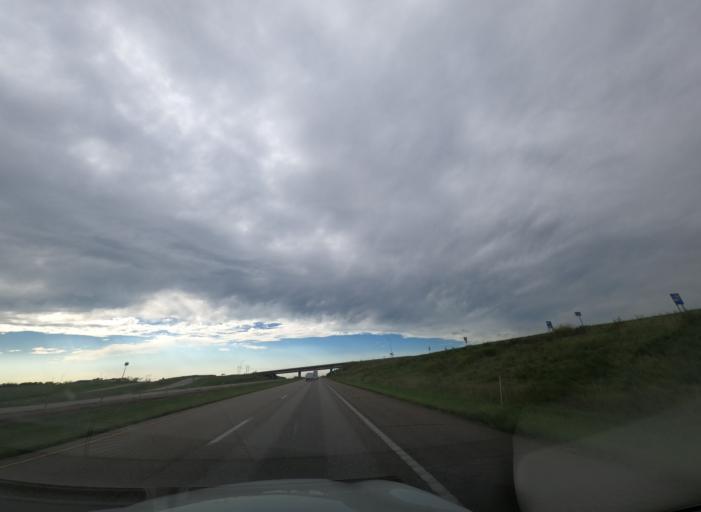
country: US
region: Missouri
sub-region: Sainte Genevieve County
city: Sainte Genevieve
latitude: 37.9352
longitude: -90.1206
